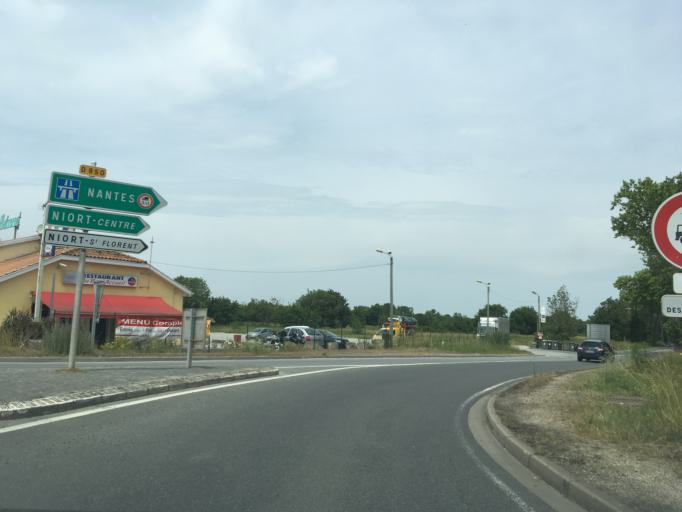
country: FR
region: Poitou-Charentes
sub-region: Departement des Deux-Sevres
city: Niort
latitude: 46.2971
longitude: -0.4657
